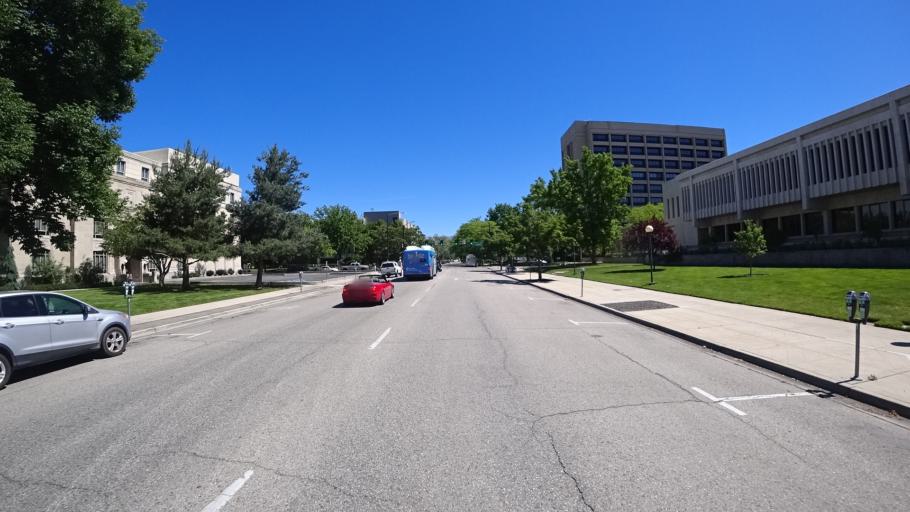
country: US
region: Idaho
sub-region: Ada County
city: Boise
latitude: 43.6162
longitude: -116.1977
